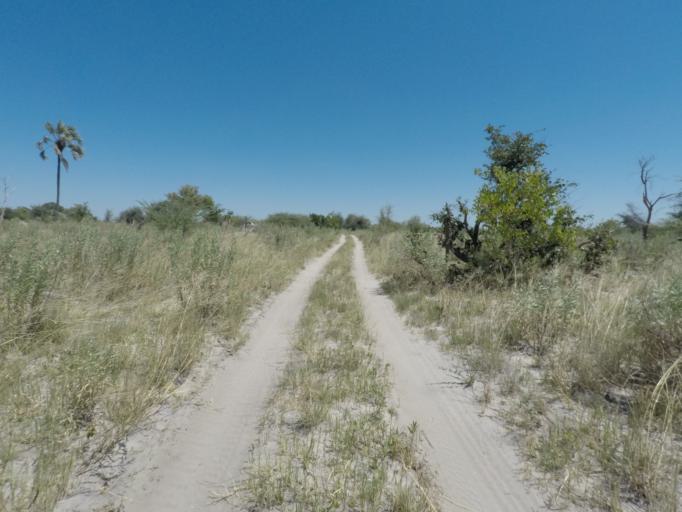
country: BW
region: North West
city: Maun
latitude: -19.4422
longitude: 23.5601
